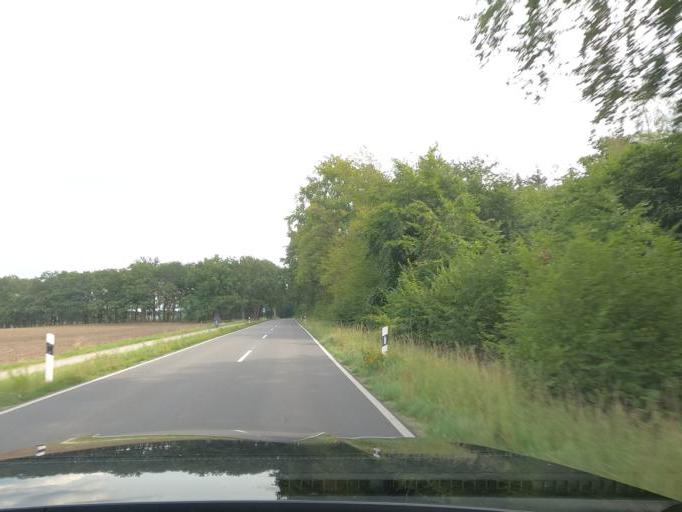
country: DE
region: Lower Saxony
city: Isernhagen Farster Bauerschaft
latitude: 52.5135
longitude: 9.8969
